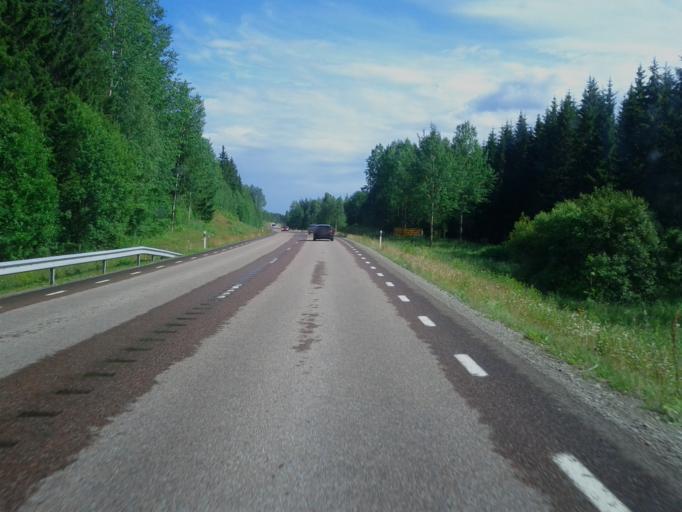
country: SE
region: Dalarna
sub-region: Faluns Kommun
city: Falun
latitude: 60.6521
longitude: 15.5590
